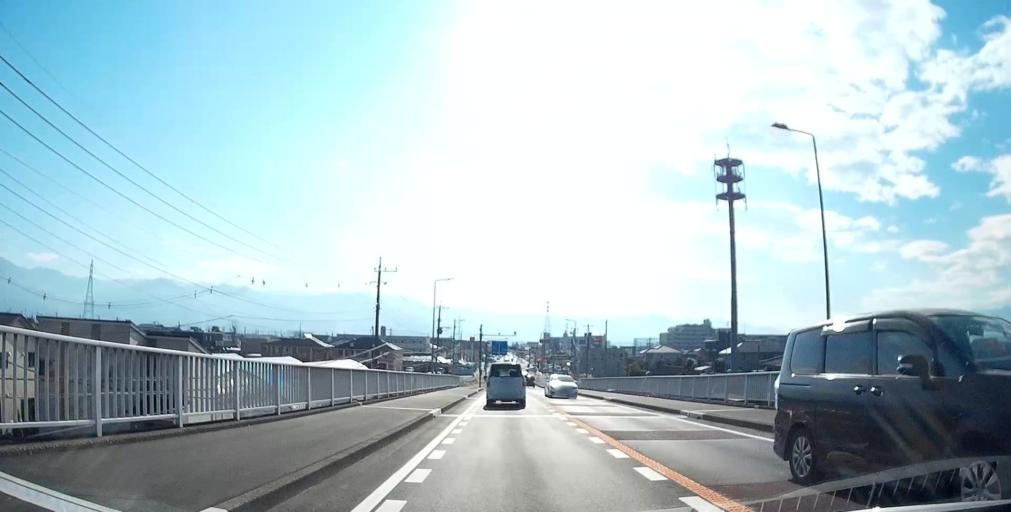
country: JP
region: Yamanashi
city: Isawa
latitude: 35.6561
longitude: 138.6144
